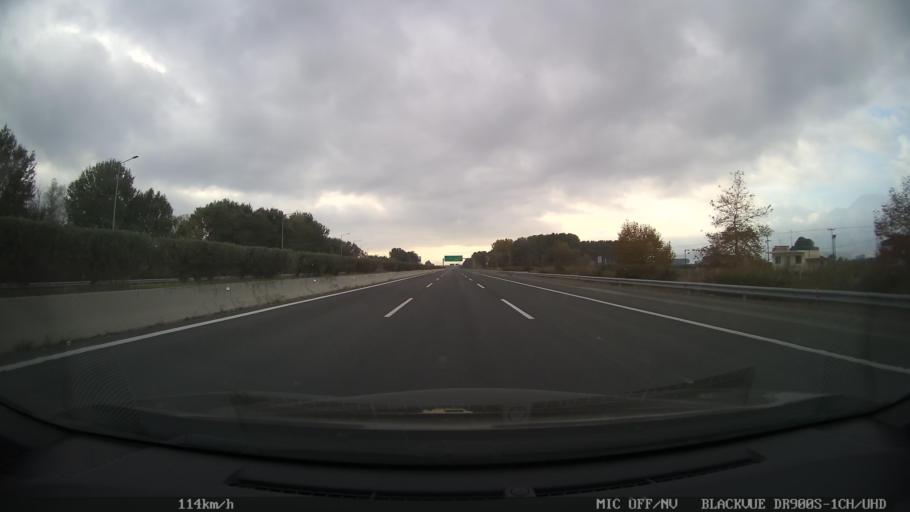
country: GR
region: Central Macedonia
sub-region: Nomos Pierias
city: Nea Efesos
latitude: 40.2056
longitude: 22.5453
